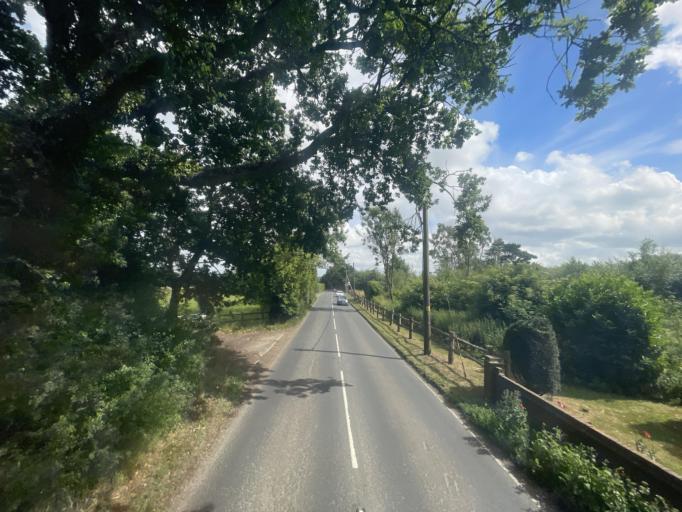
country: GB
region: England
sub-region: Kent
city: Westerham
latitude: 51.2895
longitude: 0.0584
